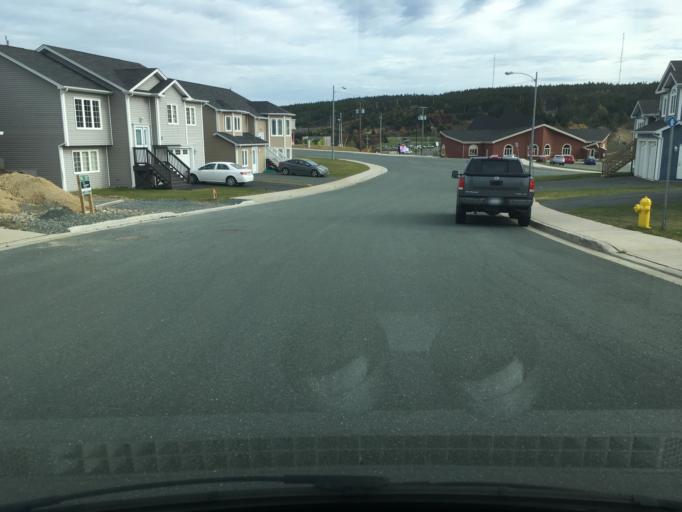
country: CA
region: Newfoundland and Labrador
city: Mount Pearl
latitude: 47.5496
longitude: -52.7866
